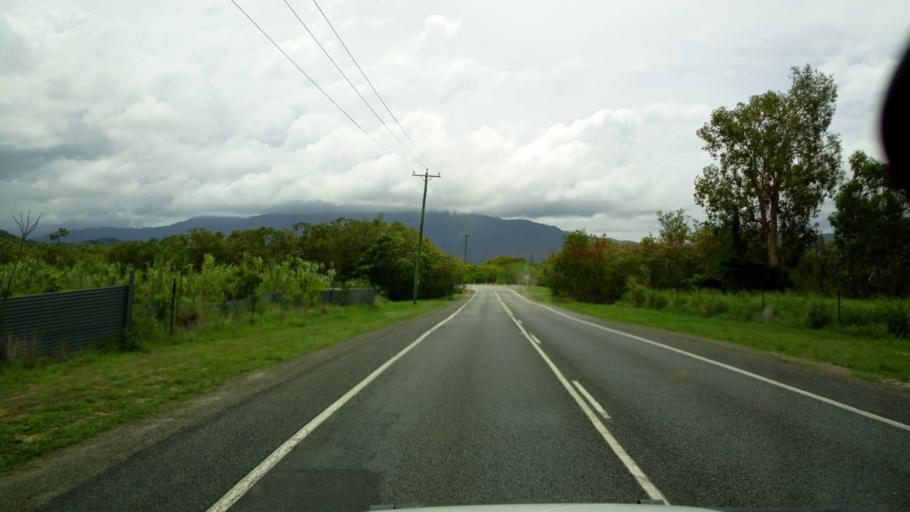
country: AU
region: Queensland
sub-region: Cairns
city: Redlynch
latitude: -16.8594
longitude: 145.7370
